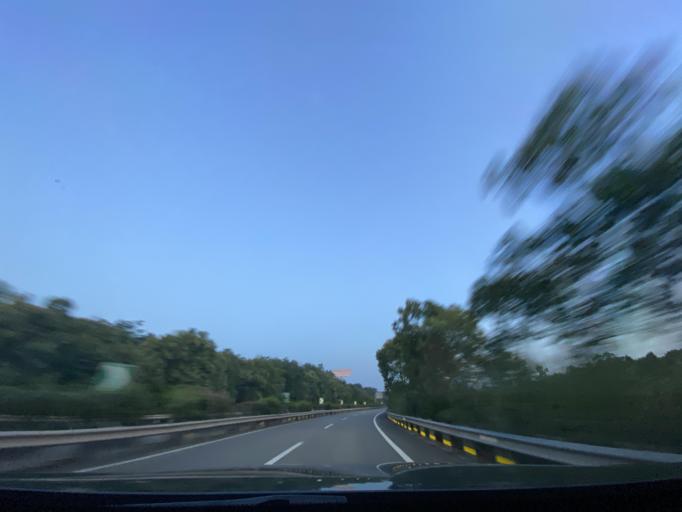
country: CN
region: Sichuan
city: Longquan
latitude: 30.4852
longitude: 104.4000
